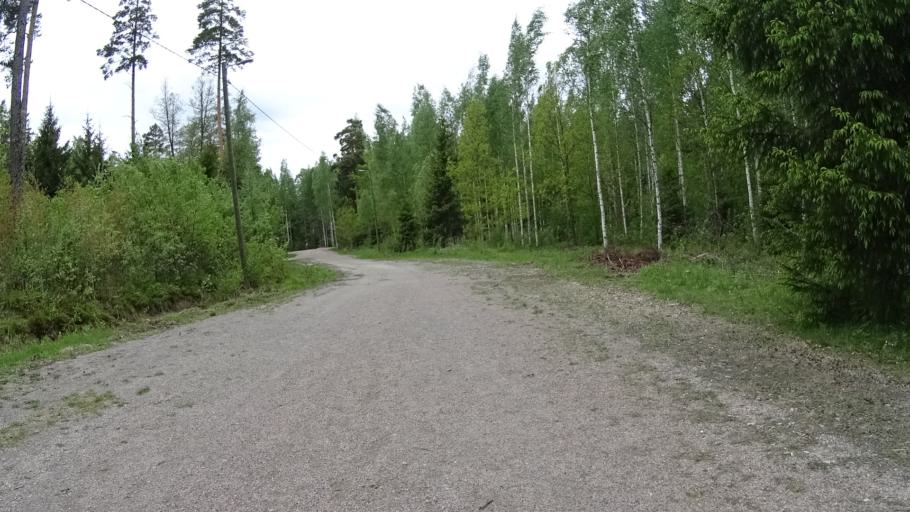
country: FI
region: Uusimaa
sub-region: Helsinki
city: Espoo
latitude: 60.2394
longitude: 24.6734
